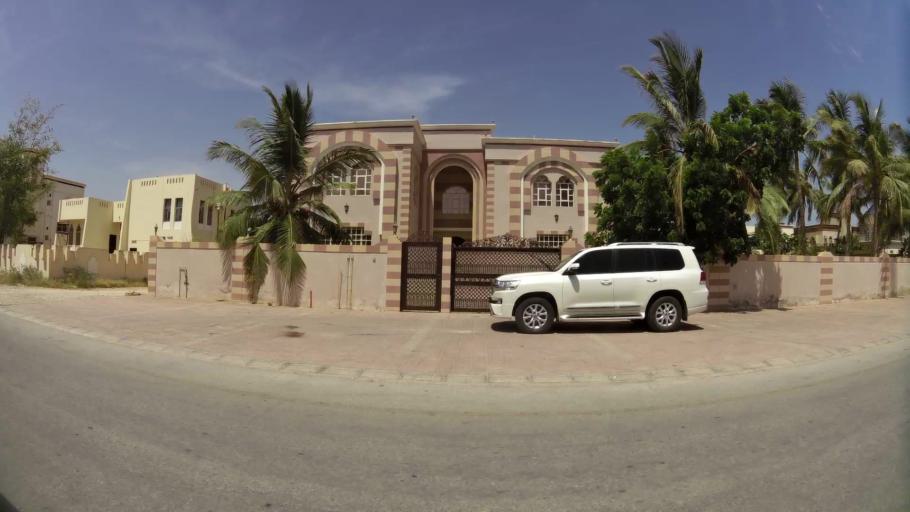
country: OM
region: Zufar
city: Salalah
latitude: 17.0557
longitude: 54.1594
